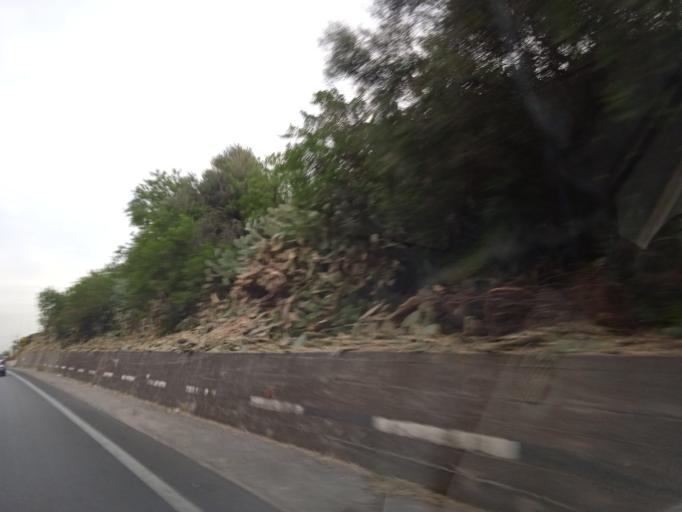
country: IT
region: Sicily
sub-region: Palermo
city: Portella di Mare
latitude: 38.0633
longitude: 13.4617
